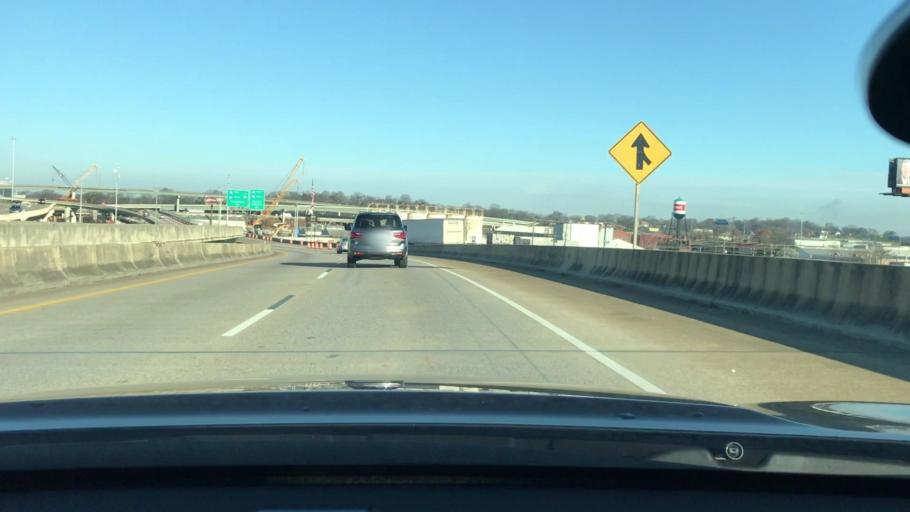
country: US
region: Alabama
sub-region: Jefferson County
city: Birmingham
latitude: 33.5236
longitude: -86.7998
